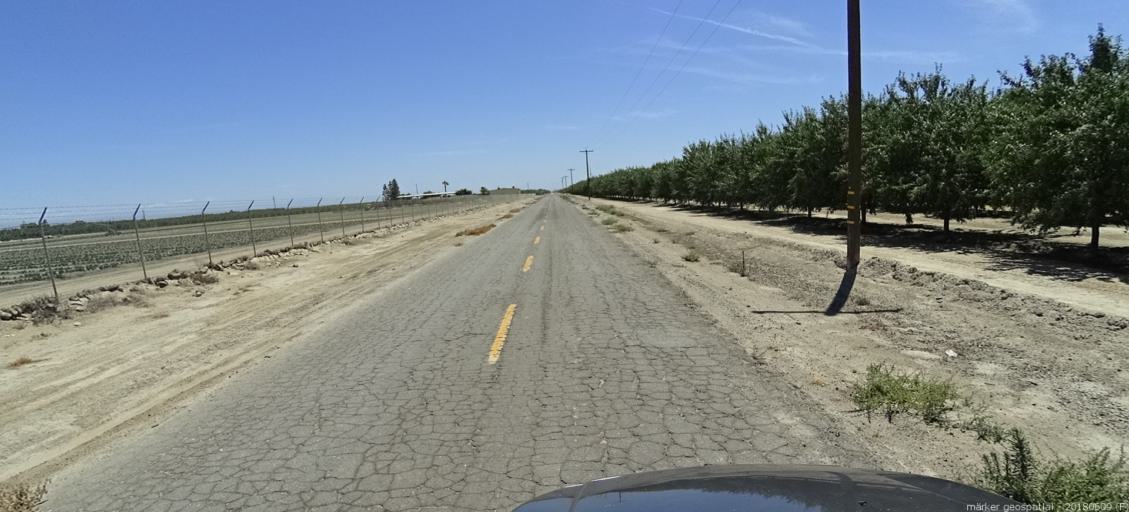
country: US
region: California
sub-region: Madera County
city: Fairmead
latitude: 36.9382
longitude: -120.2060
